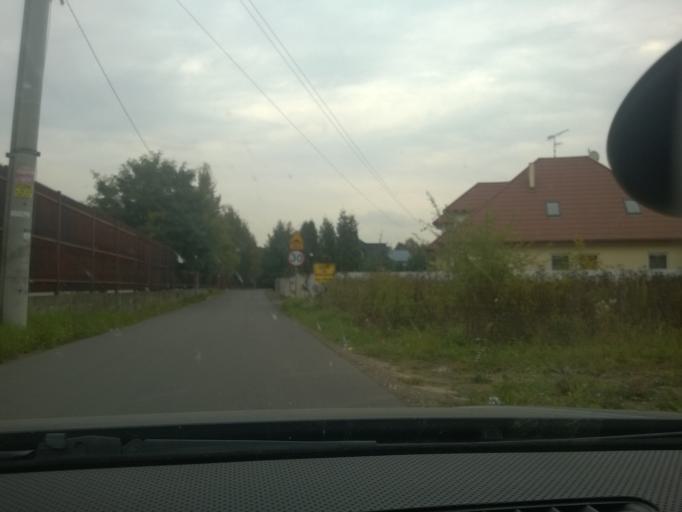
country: PL
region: Masovian Voivodeship
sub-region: Powiat warszawski zachodni
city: Kielpin
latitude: 52.3571
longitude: 20.8613
